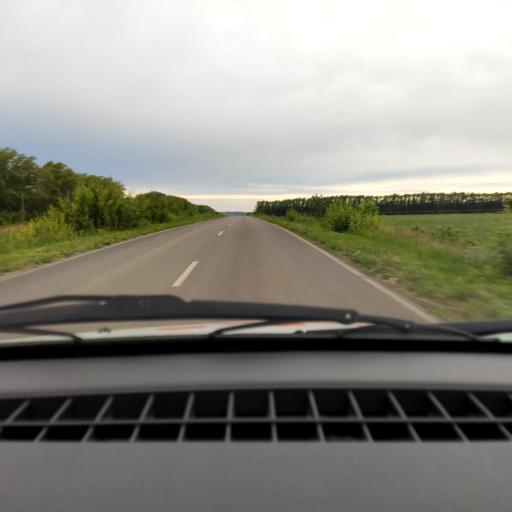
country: RU
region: Bashkortostan
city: Avdon
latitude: 54.5195
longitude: 55.7720
